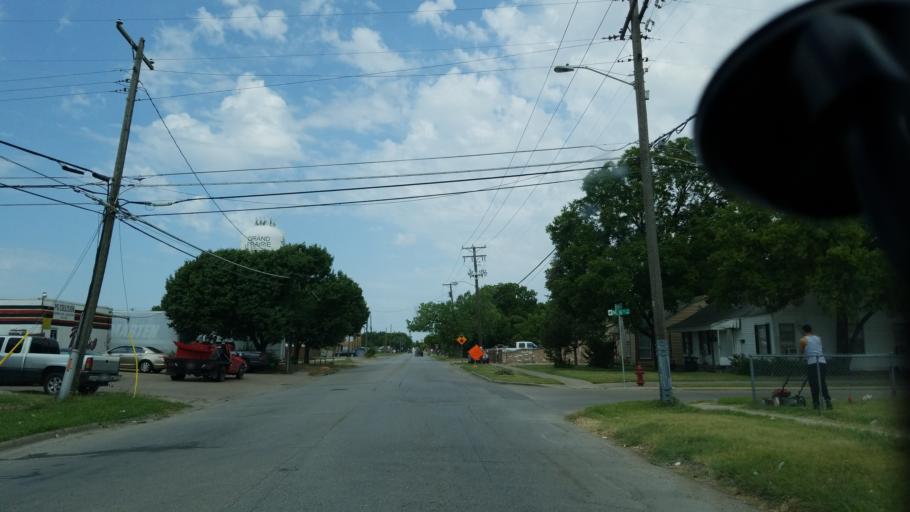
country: US
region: Texas
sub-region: Dallas County
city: Grand Prairie
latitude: 32.7487
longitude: -96.9840
